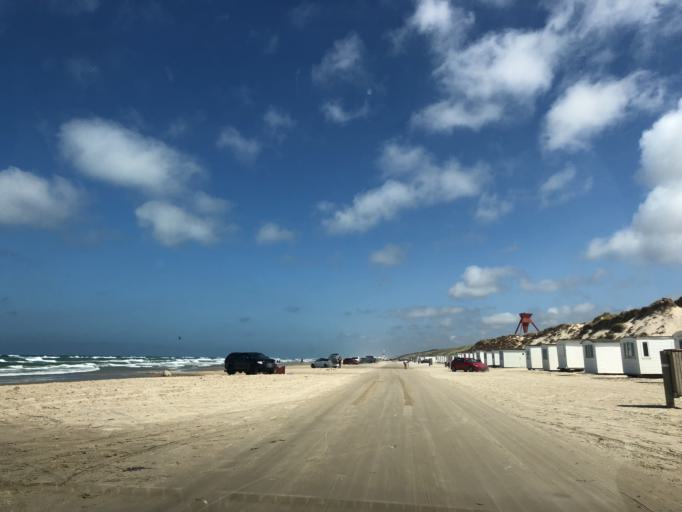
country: DK
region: North Denmark
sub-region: Jammerbugt Kommune
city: Pandrup
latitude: 57.2522
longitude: 9.5758
